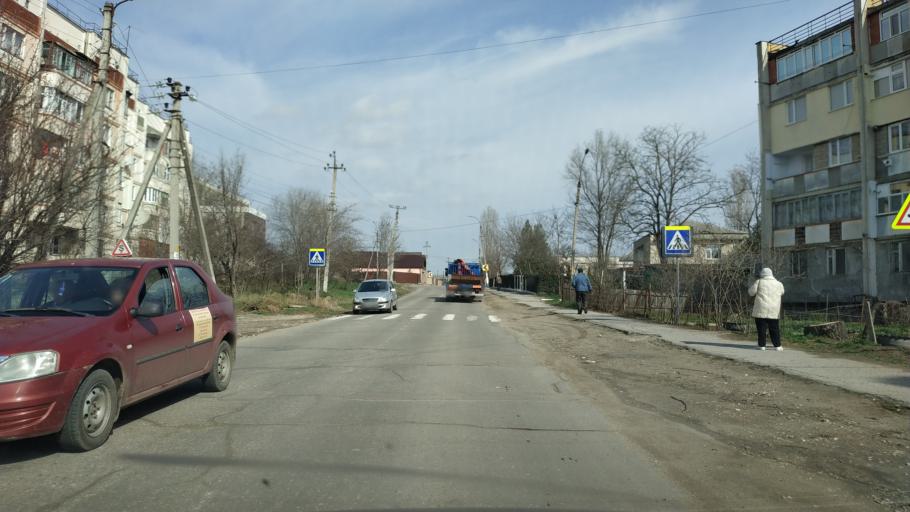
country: MD
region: Gagauzia
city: Vulcanesti
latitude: 45.6880
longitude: 28.4057
